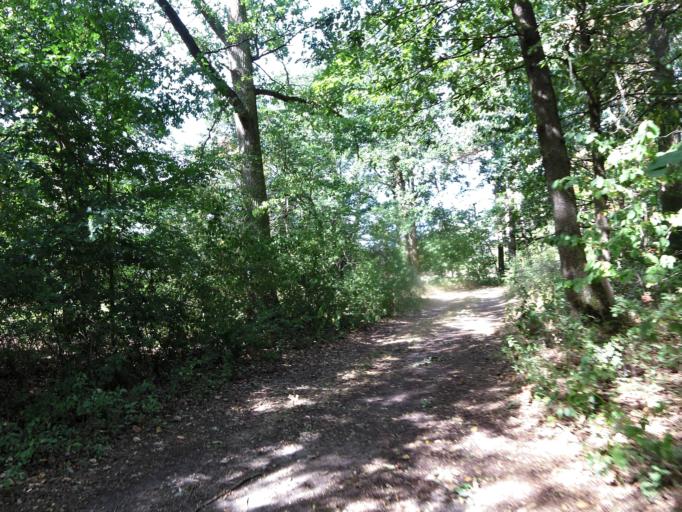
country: DE
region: Bavaria
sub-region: Regierungsbezirk Unterfranken
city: Eibelstadt
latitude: 49.7443
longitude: 10.0095
